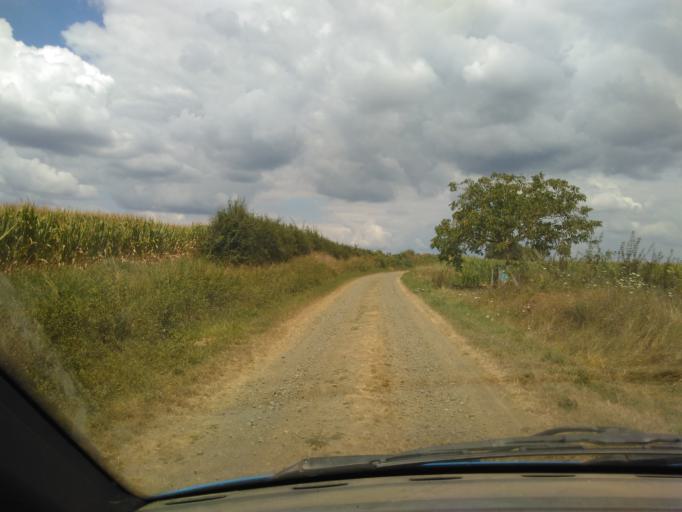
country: FR
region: Pays de la Loire
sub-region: Departement de la Vendee
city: Sainte-Hermine
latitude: 46.5699
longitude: -1.0248
